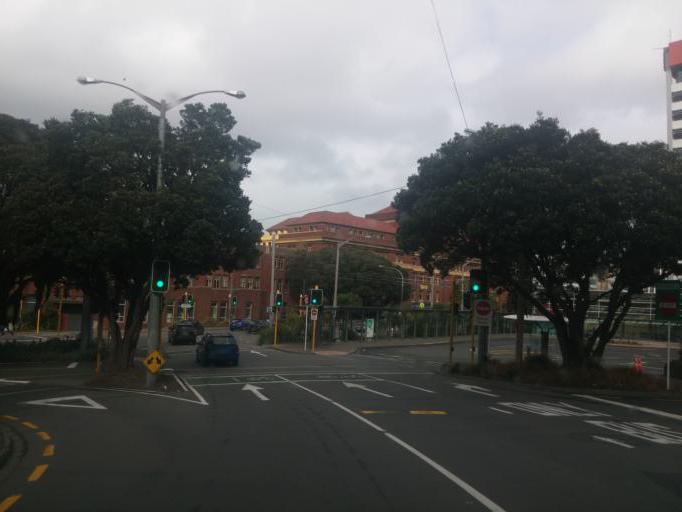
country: NZ
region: Wellington
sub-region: Wellington City
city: Wellington
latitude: -41.2776
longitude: 174.7798
